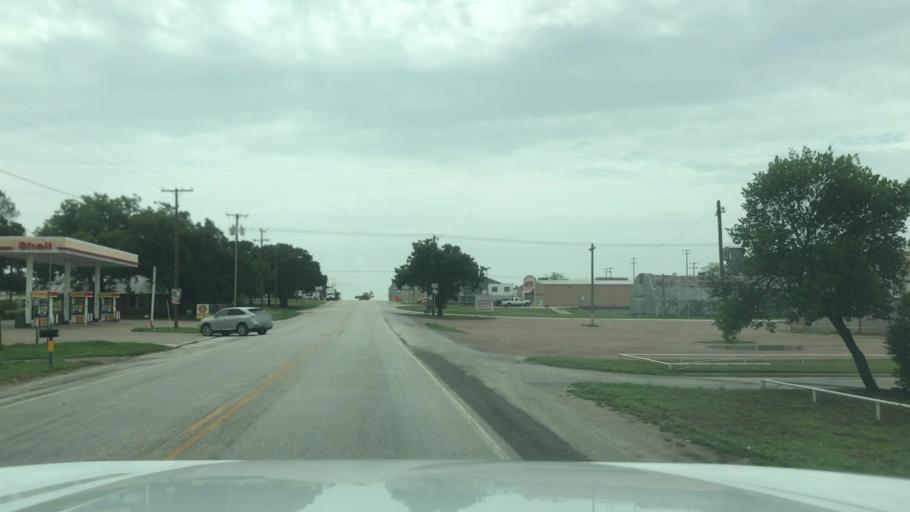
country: US
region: Texas
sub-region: Eastland County
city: Gorman
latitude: 32.2119
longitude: -98.6685
